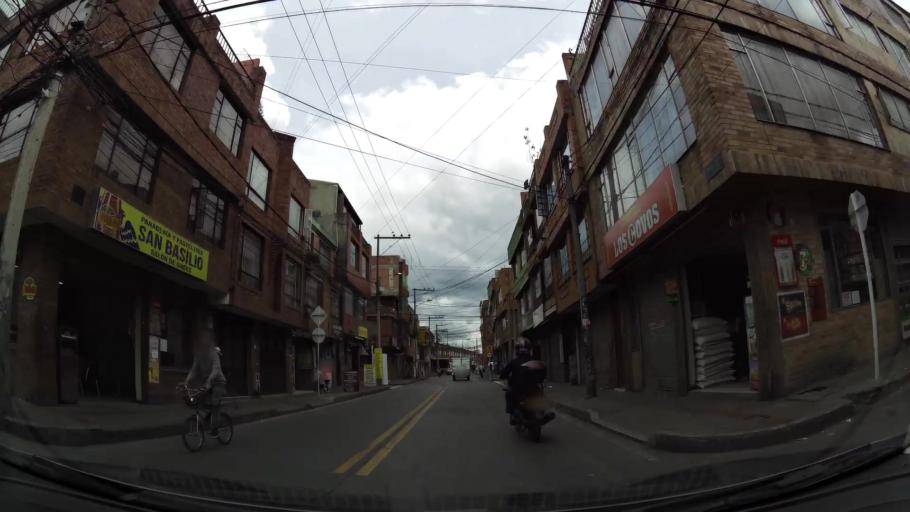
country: CO
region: Cundinamarca
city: Funza
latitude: 4.7032
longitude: -74.1229
